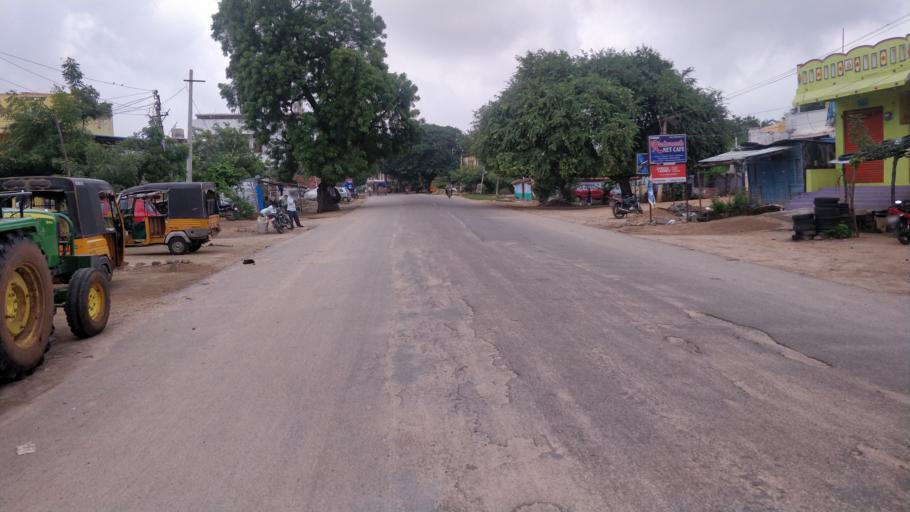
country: IN
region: Telangana
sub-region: Medak
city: Narsingi
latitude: 18.1856
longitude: 78.3980
